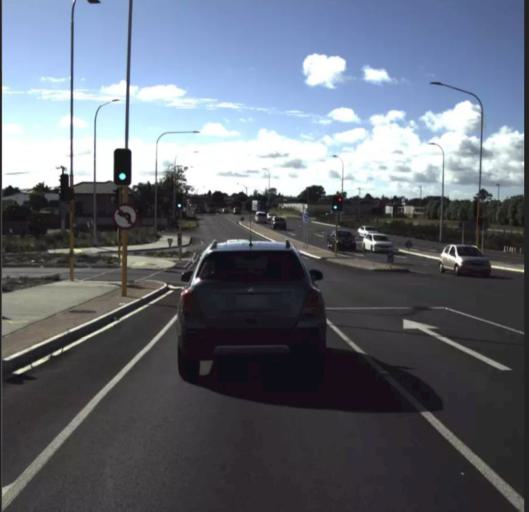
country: NZ
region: Auckland
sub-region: Auckland
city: Rosebank
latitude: -36.8563
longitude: 174.6518
